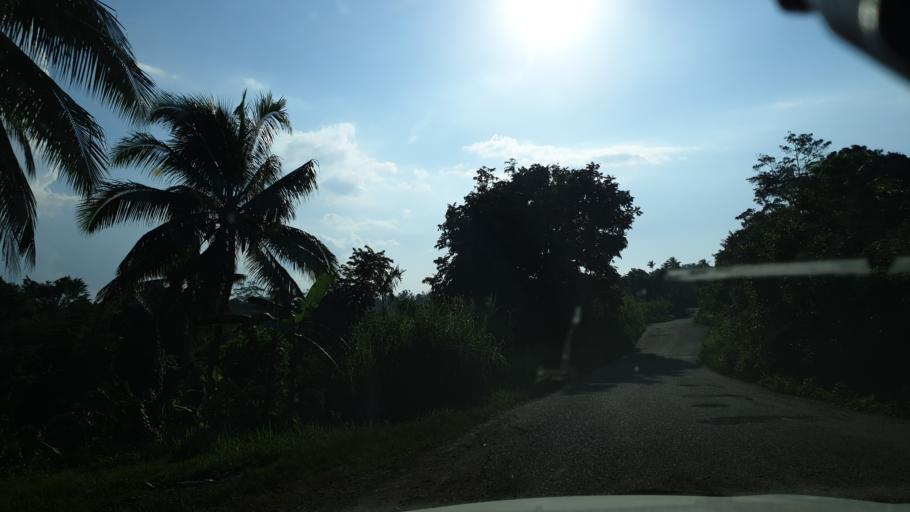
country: PG
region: East Sepik
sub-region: Wewak
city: Wewak
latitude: -3.6964
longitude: 143.6494
